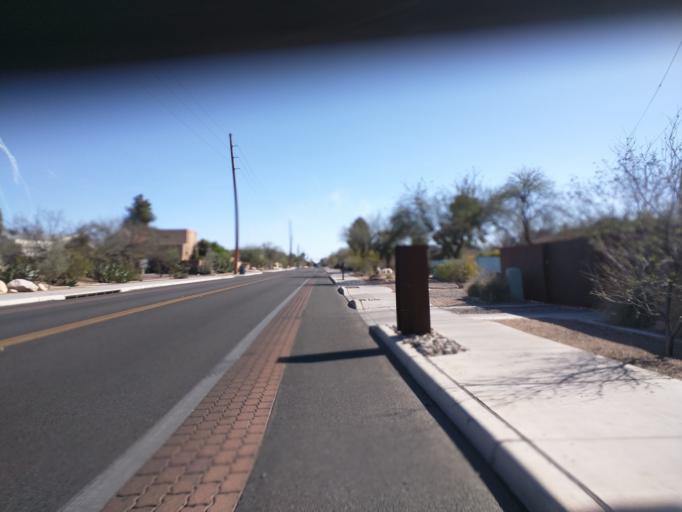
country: US
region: Arizona
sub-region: Pima County
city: Catalina Foothills
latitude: 32.2755
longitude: -110.9525
